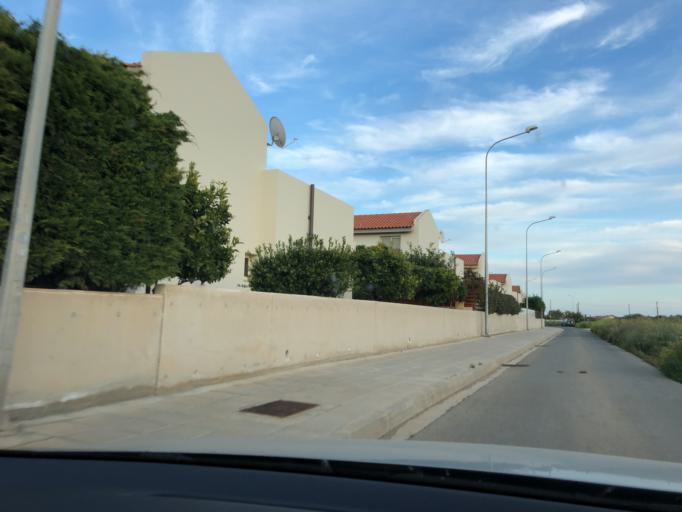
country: CY
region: Larnaka
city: Perivolia
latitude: 34.8351
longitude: 33.6023
